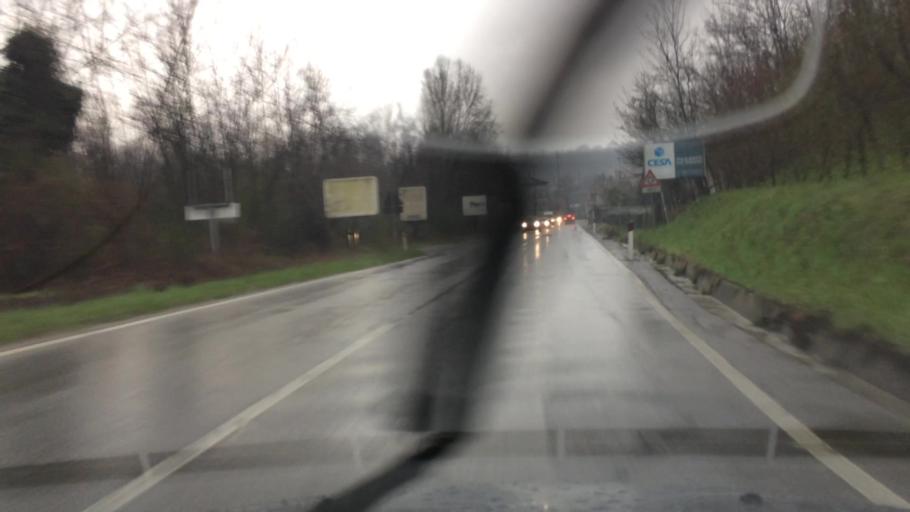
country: IT
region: Lombardy
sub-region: Provincia di Como
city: Montesolaro
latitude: 45.7214
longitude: 9.1032
